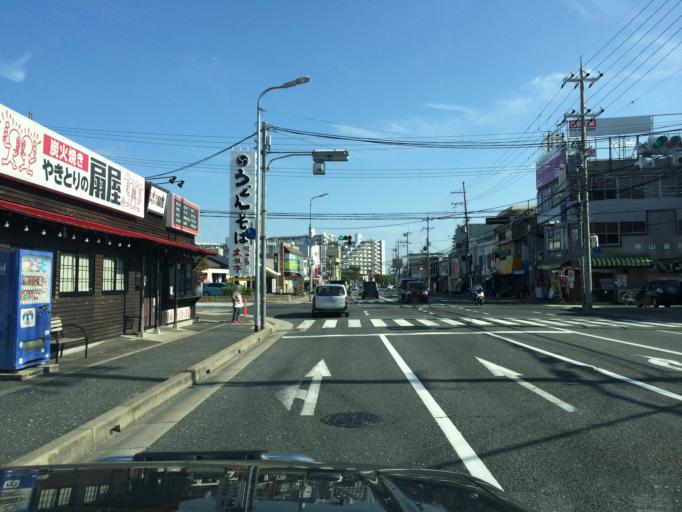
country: JP
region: Hyogo
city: Itami
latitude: 34.7902
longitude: 135.3802
